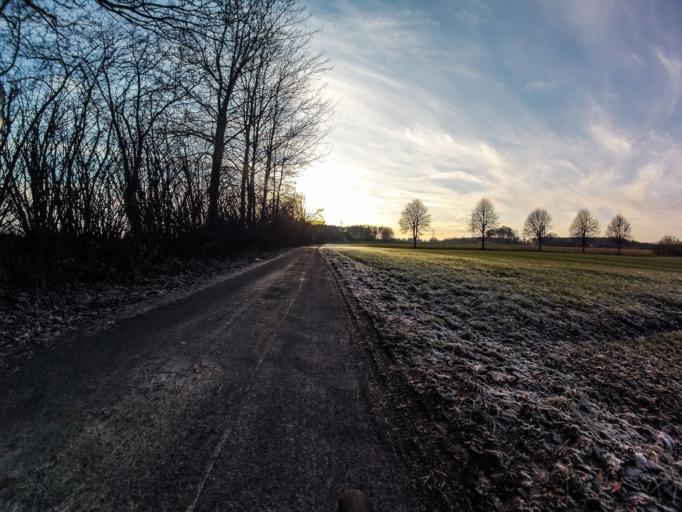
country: DE
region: North Rhine-Westphalia
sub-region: Regierungsbezirk Munster
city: Mettingen
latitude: 52.2847
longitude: 7.8036
